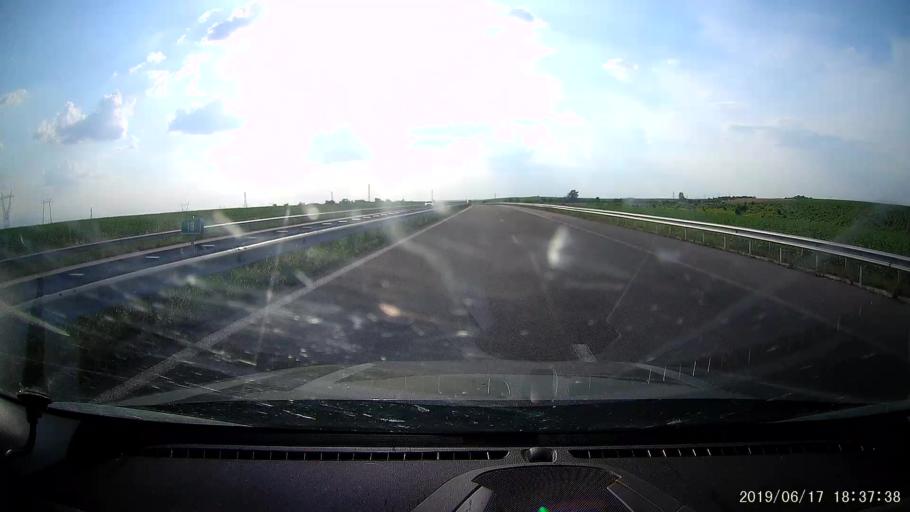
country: BG
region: Stara Zagora
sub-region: Obshtina Chirpan
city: Chirpan
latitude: 42.1323
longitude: 25.3559
